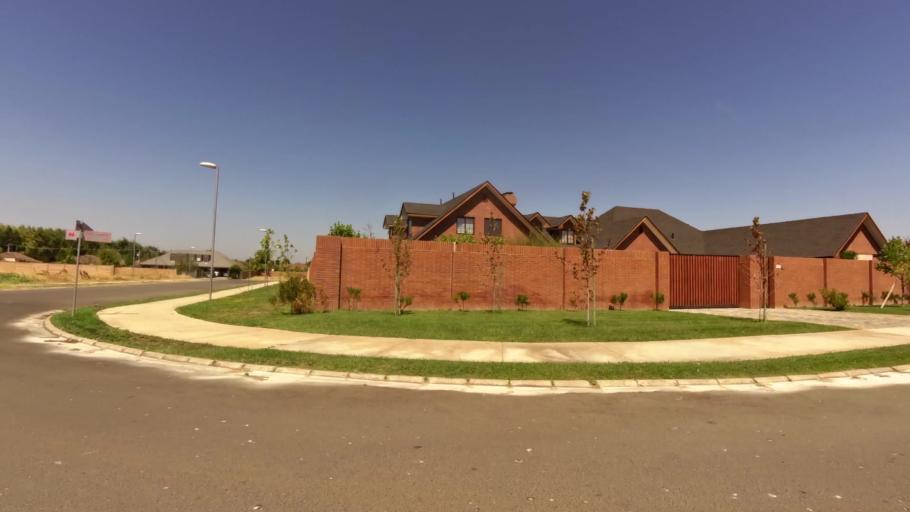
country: CL
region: Maule
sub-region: Provincia de Talca
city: Talca
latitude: -35.4294
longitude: -71.6000
